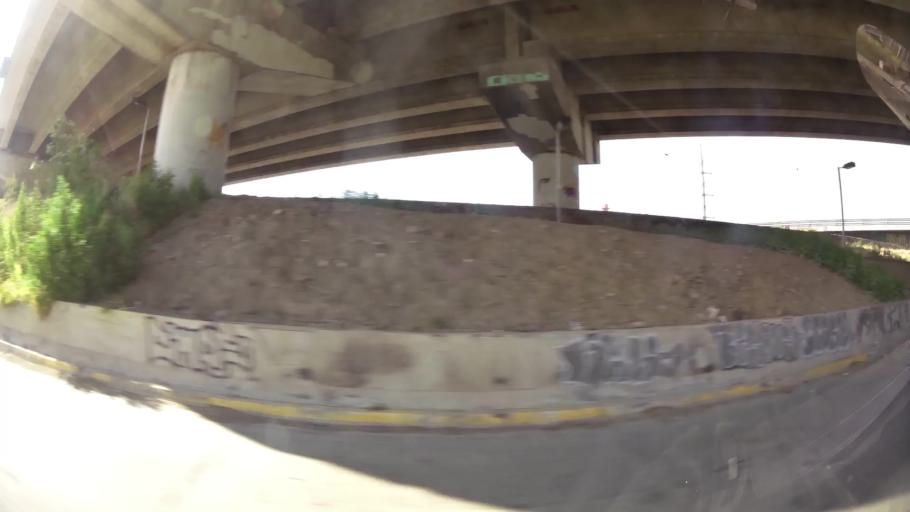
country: CL
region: Santiago Metropolitan
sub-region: Provincia de Santiago
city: Lo Prado
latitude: -33.4185
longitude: -70.6913
